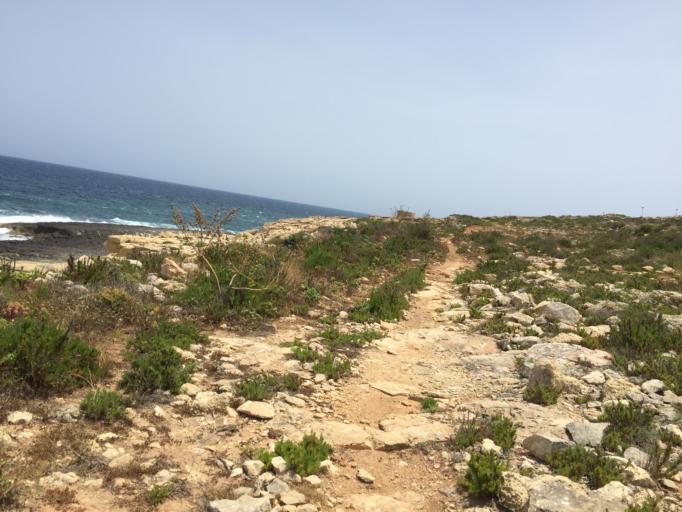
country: MT
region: Ix-Xghajra
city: Xghajra
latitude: 35.8804
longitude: 14.5598
